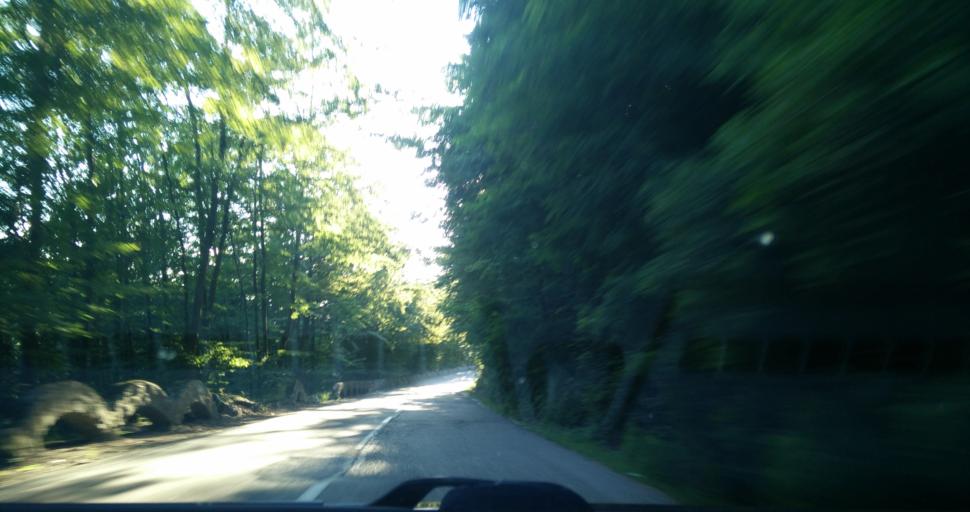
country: RO
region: Bihor
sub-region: Oras Nucet
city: Nucet
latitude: 46.4813
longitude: 22.5986
